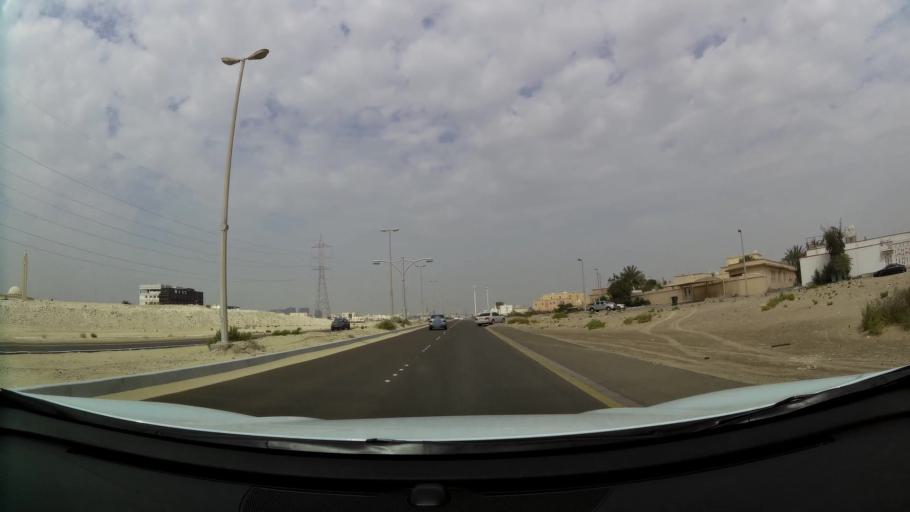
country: AE
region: Abu Dhabi
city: Abu Dhabi
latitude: 24.3178
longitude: 54.6341
